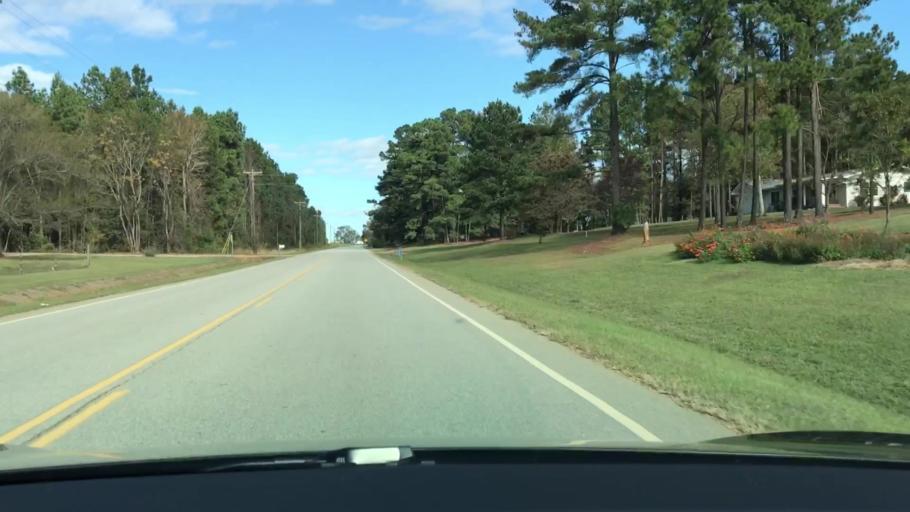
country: US
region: Georgia
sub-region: Jefferson County
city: Wrens
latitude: 33.1351
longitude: -82.4541
